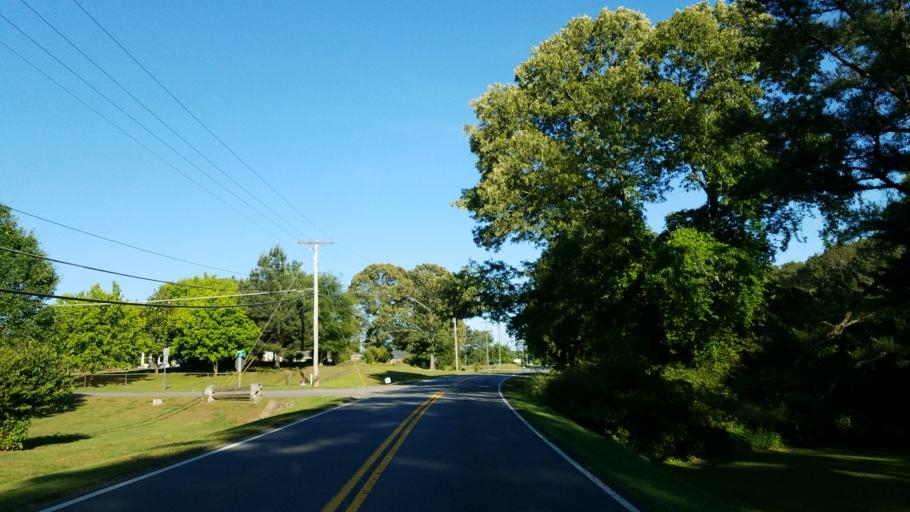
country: US
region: Georgia
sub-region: Cherokee County
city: Holly Springs
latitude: 34.1739
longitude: -84.4809
